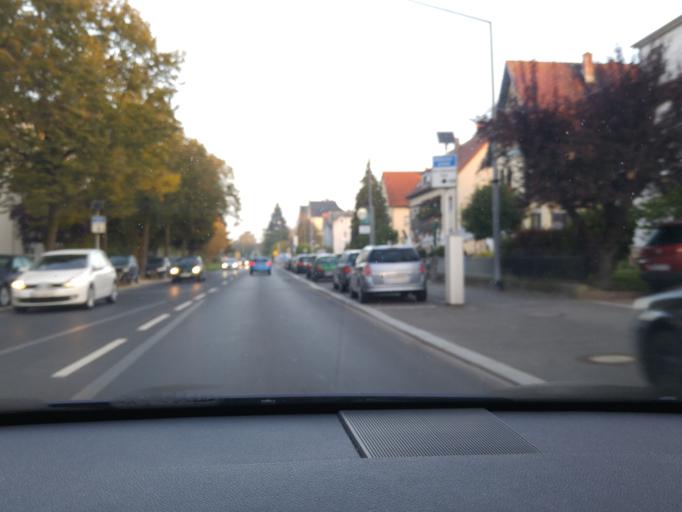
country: DE
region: Hesse
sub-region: Regierungsbezirk Darmstadt
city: Bad Nauheim
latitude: 50.3712
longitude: 8.7443
